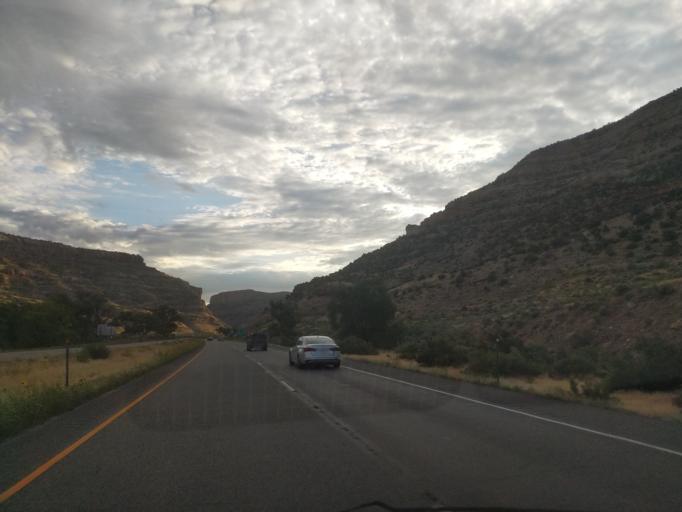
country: US
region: Colorado
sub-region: Mesa County
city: Palisade
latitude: 39.1699
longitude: -108.2961
